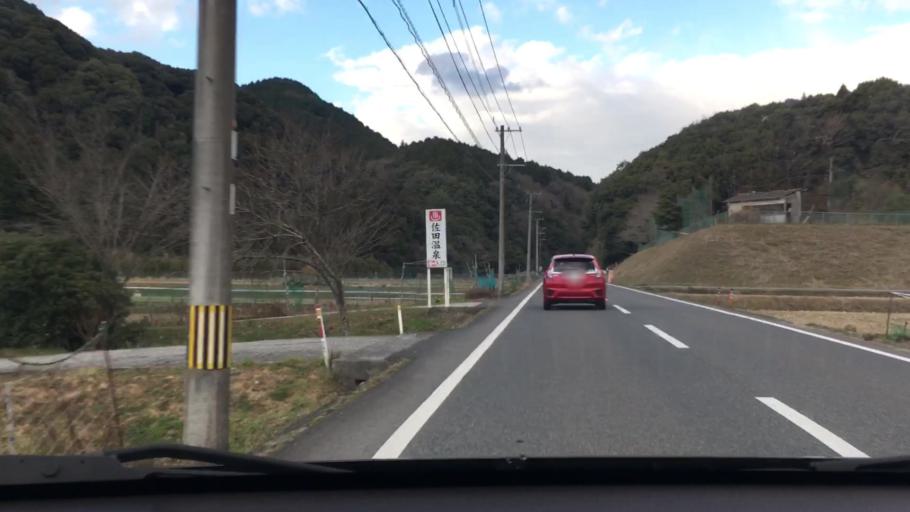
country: JP
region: Oita
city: Bungo-Takada-shi
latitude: 33.4509
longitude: 131.3931
